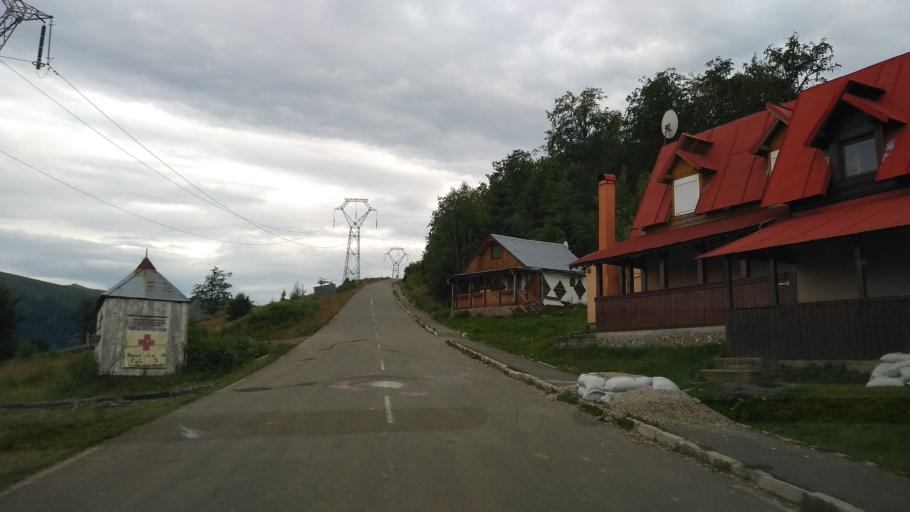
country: RO
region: Hunedoara
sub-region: Municipiul  Vulcan
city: Jiu-Paroseni
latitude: 45.3282
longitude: 23.2879
